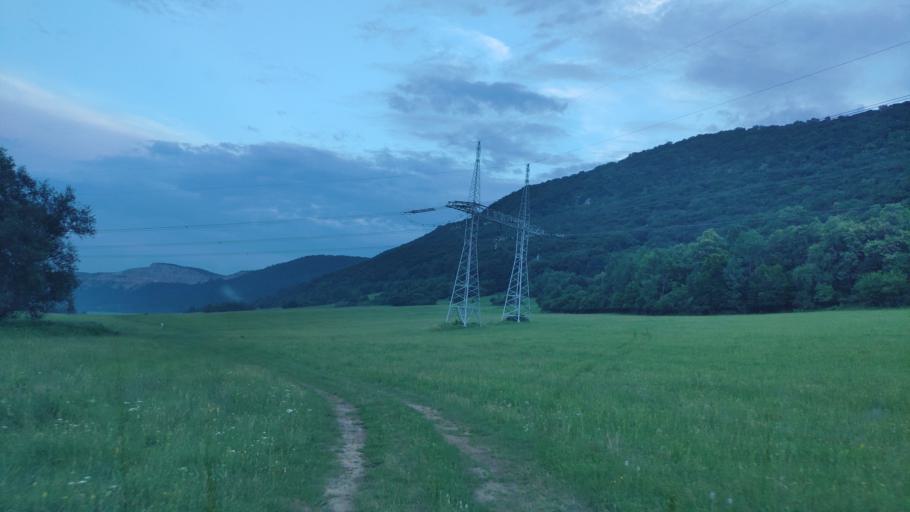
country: SK
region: Kosicky
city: Medzev
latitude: 48.5836
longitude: 20.7671
